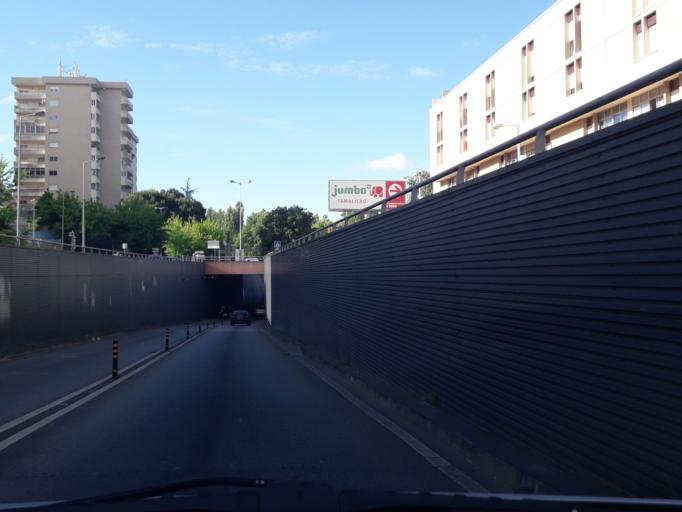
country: PT
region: Braga
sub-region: Vila Nova de Famalicao
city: Vila Nova de Famalicao
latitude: 41.4085
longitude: -8.5166
